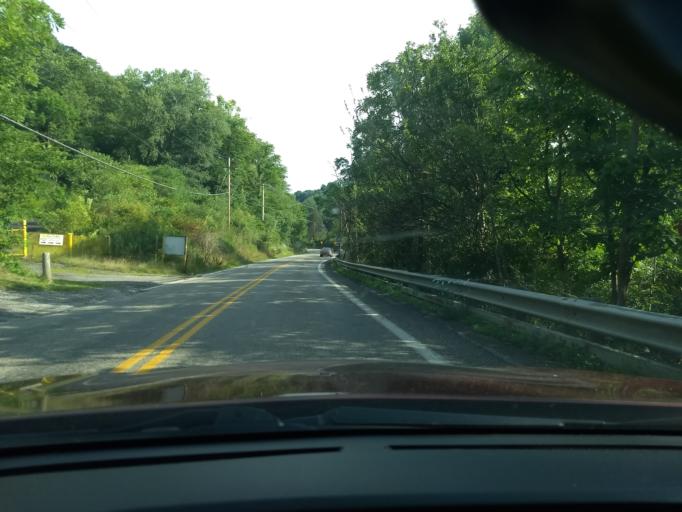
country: US
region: Pennsylvania
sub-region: Allegheny County
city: Tarentum
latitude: 40.6196
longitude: -79.7631
